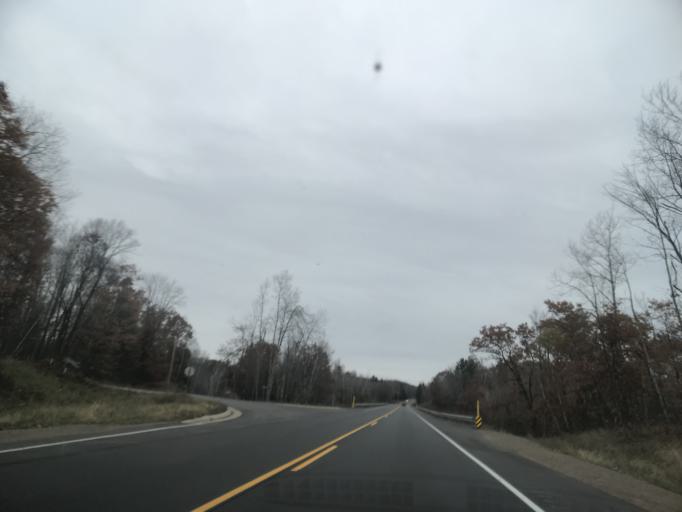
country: US
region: Wisconsin
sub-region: Menominee County
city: Legend Lake
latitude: 45.2732
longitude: -88.5087
